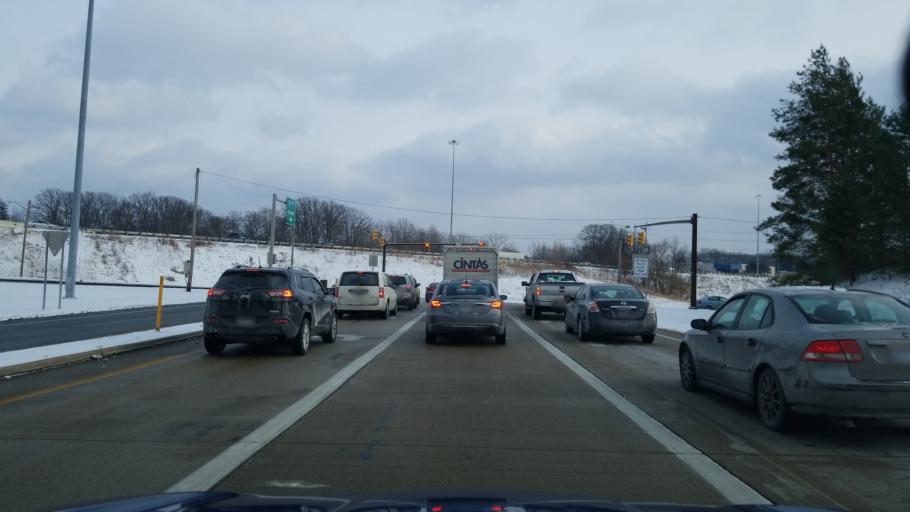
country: US
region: Ohio
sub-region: Cuyahoga County
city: Middleburg Heights
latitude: 41.3546
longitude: -81.8206
